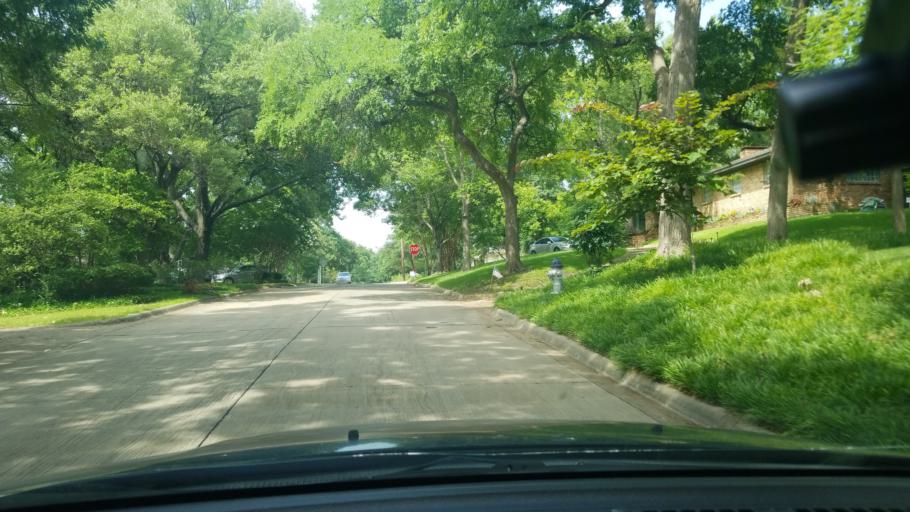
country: US
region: Texas
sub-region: Dallas County
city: Highland Park
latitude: 32.8119
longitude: -96.7129
